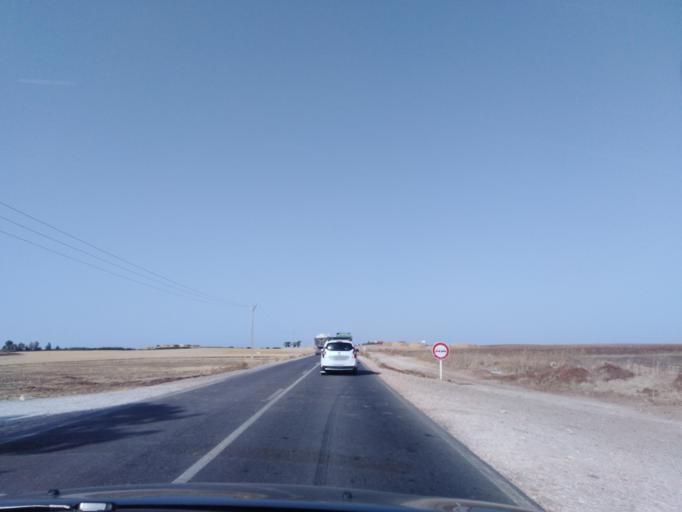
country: MA
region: Doukkala-Abda
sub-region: Safi
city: Safi
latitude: 32.2696
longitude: -8.9430
